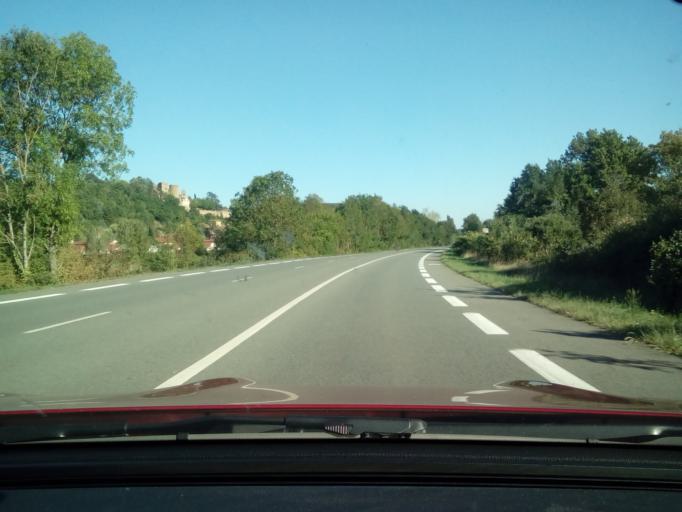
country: FR
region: Rhone-Alpes
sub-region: Departement du Rhone
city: Chessy
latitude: 45.8808
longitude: 4.6361
